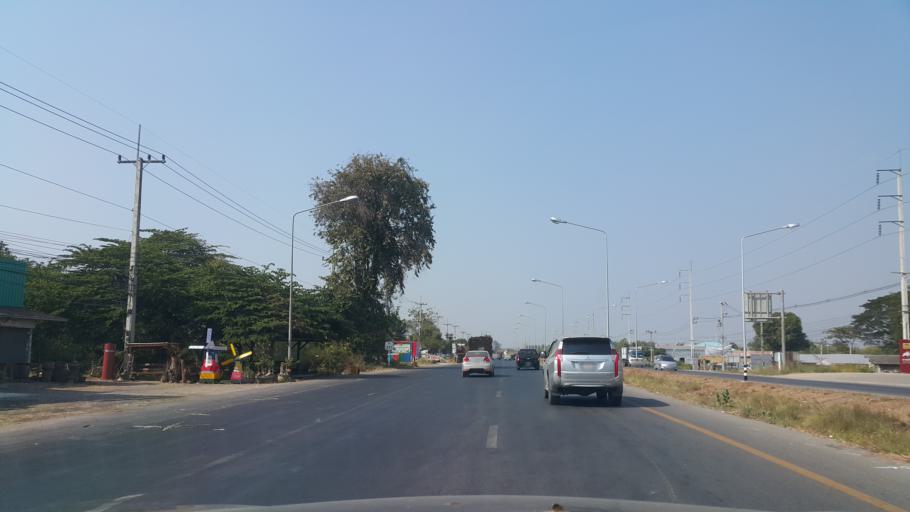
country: TH
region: Chaiyaphum
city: Phu Khiao
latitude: 16.4254
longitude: 102.1299
